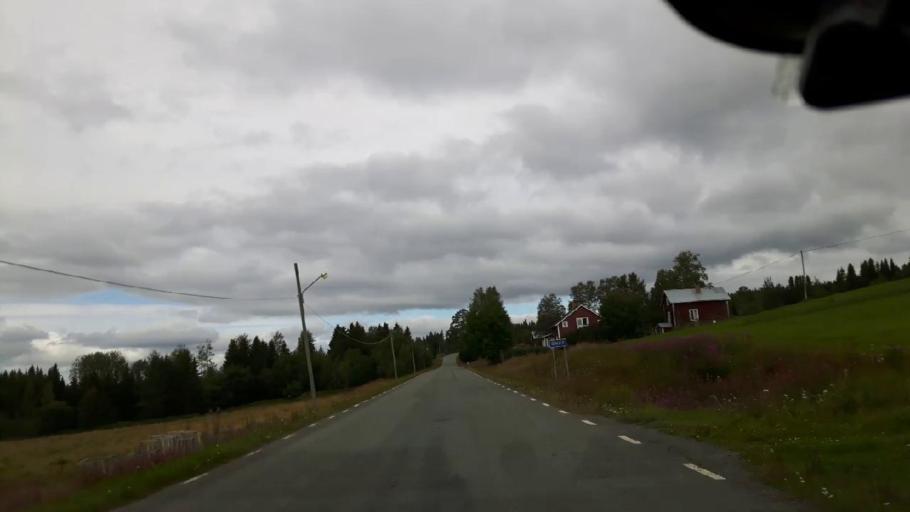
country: SE
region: Jaemtland
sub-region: Krokoms Kommun
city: Valla
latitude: 63.5107
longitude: 13.8869
